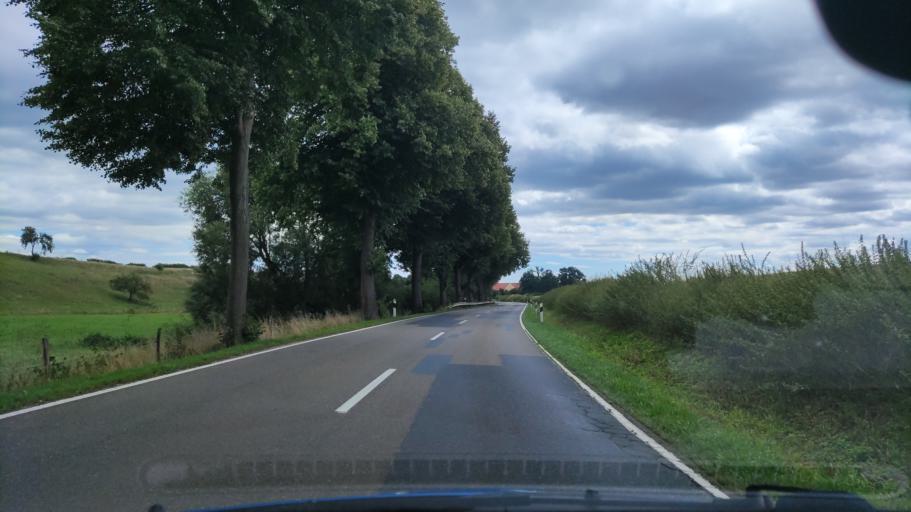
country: DE
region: Lower Saxony
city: Eimen
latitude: 51.8291
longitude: 9.8064
